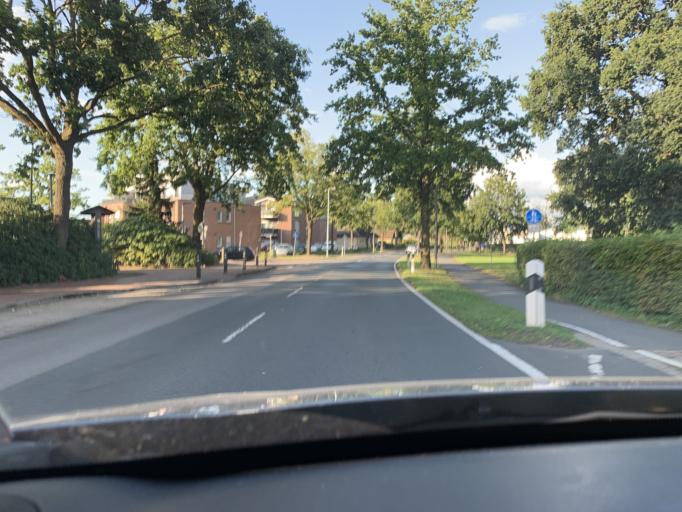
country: DE
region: Lower Saxony
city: Edewecht
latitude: 53.1367
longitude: 7.9868
